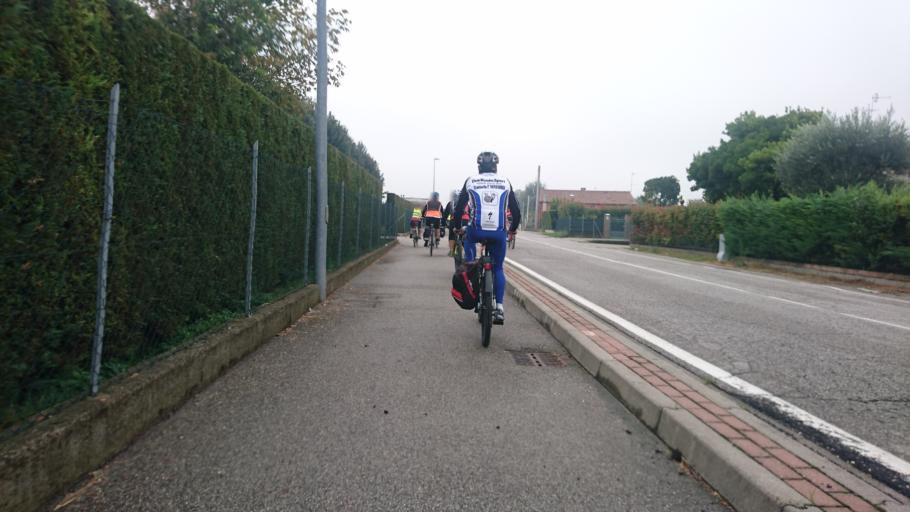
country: IT
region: Veneto
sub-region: Provincia di Padova
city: Pozzonovo
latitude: 45.2036
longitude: 11.7833
